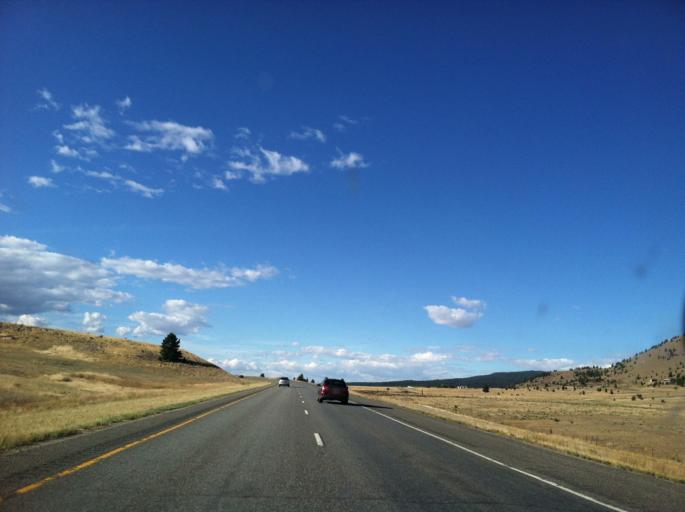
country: US
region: Montana
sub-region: Silver Bow County
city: Butte-Silver Bow (Balance)
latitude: 46.0358
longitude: -112.7328
